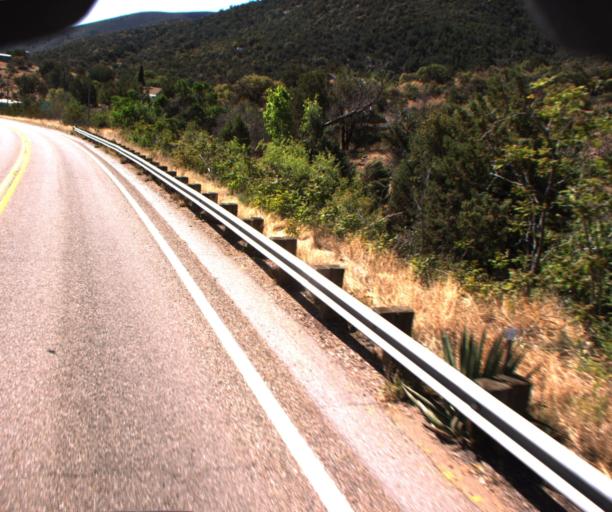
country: US
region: Arizona
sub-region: Cochise County
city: Bisbee
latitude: 31.4541
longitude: -109.9390
